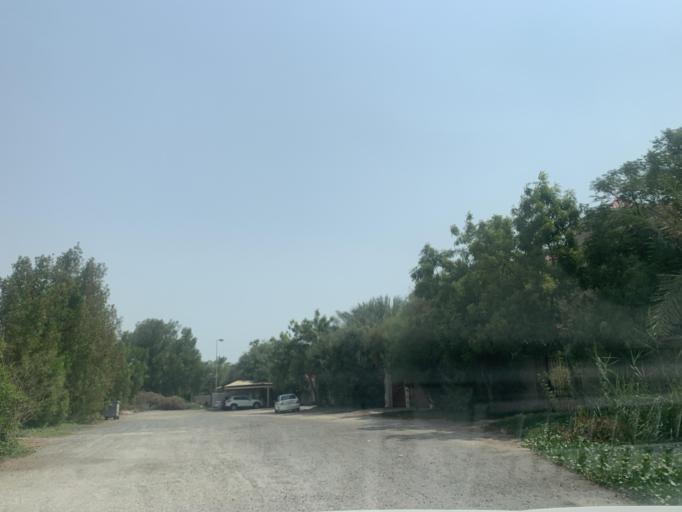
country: BH
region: Central Governorate
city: Madinat Hamad
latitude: 26.1604
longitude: 50.4540
